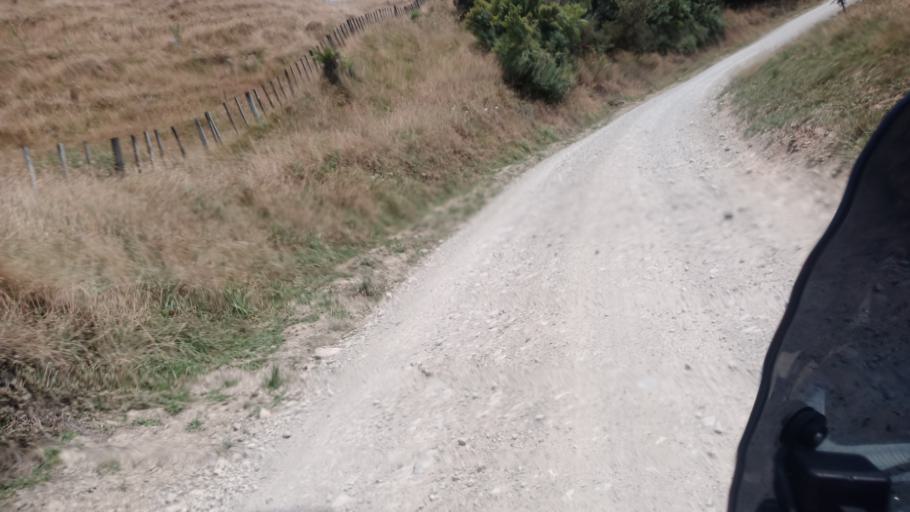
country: NZ
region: Bay of Plenty
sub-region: Opotiki District
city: Opotiki
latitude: -37.6549
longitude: 178.1311
